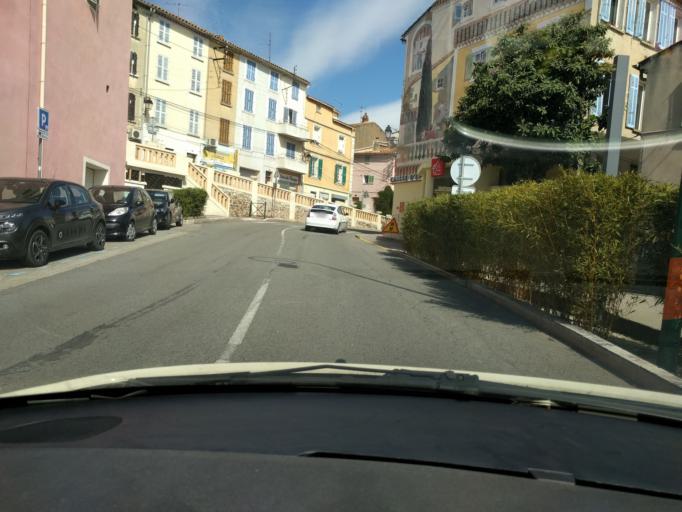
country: FR
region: Provence-Alpes-Cote d'Azur
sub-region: Departement du Var
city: Pierrefeu-du-Var
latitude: 43.2264
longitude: 6.1430
